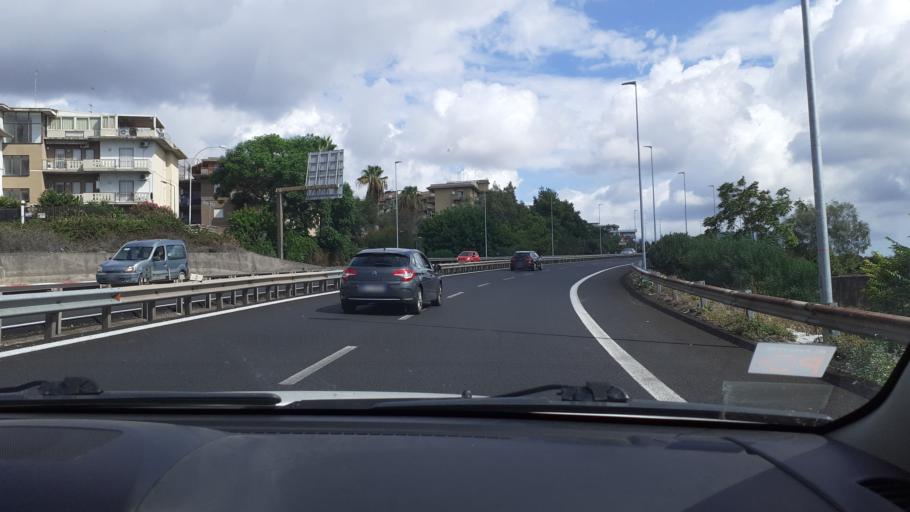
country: IT
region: Sicily
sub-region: Catania
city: Canalicchio
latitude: 37.5327
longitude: 15.0949
